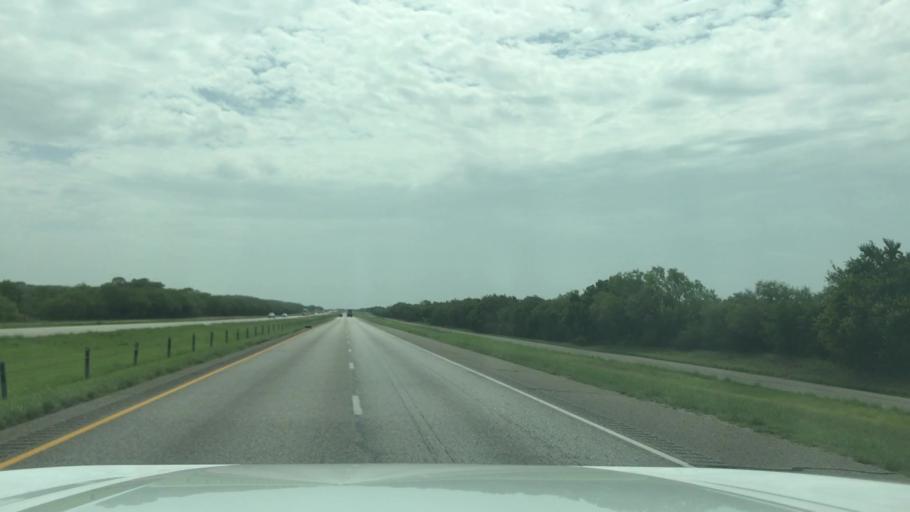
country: US
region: Texas
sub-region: Callahan County
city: Baird
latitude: 32.3753
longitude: -99.2418
